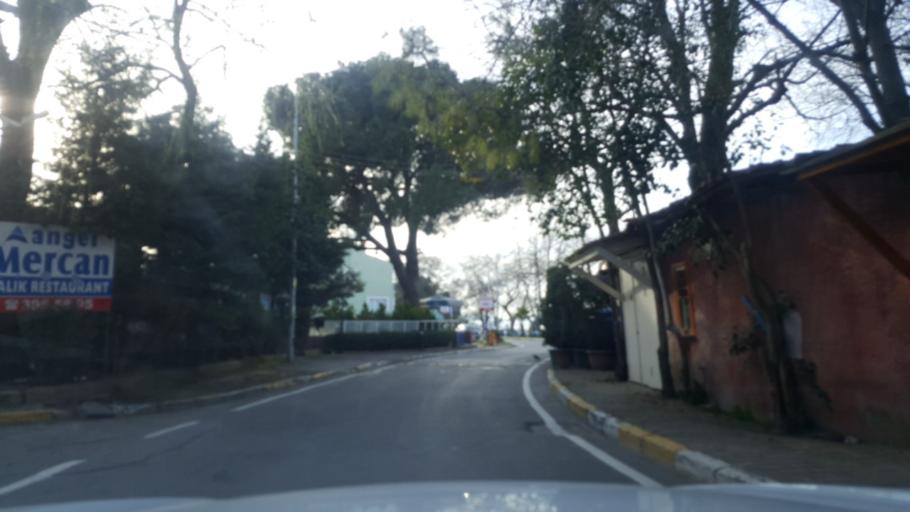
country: TR
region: Istanbul
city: Icmeler
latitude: 40.8198
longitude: 29.2751
